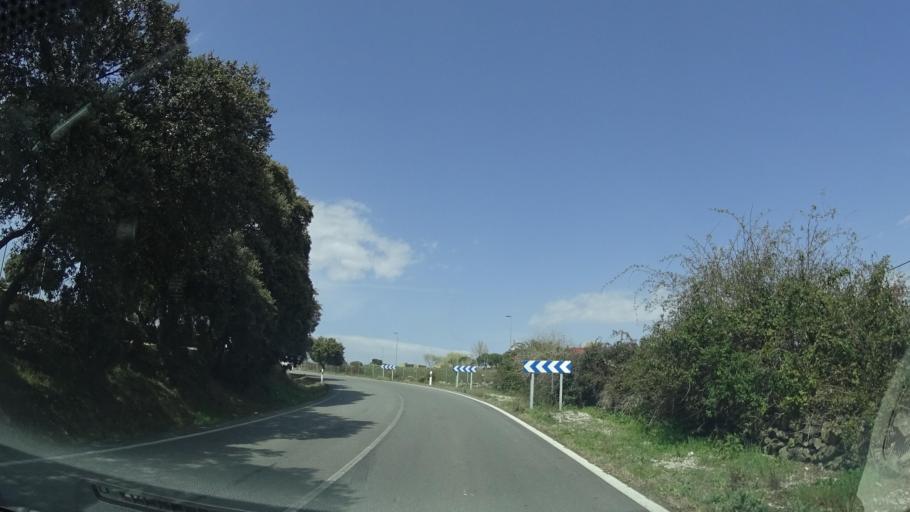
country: ES
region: Madrid
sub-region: Provincia de Madrid
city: Colmenar Viejo
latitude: 40.6932
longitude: -3.7689
